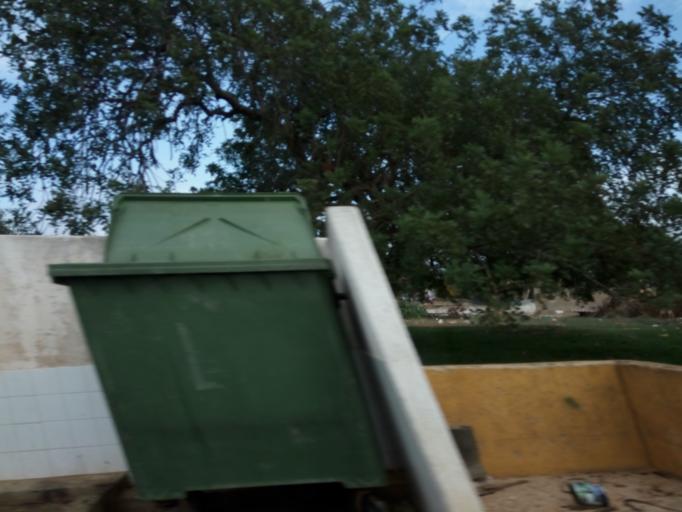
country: PT
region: Faro
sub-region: Faro
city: Santa Barbara de Nexe
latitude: 37.0911
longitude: -7.9612
